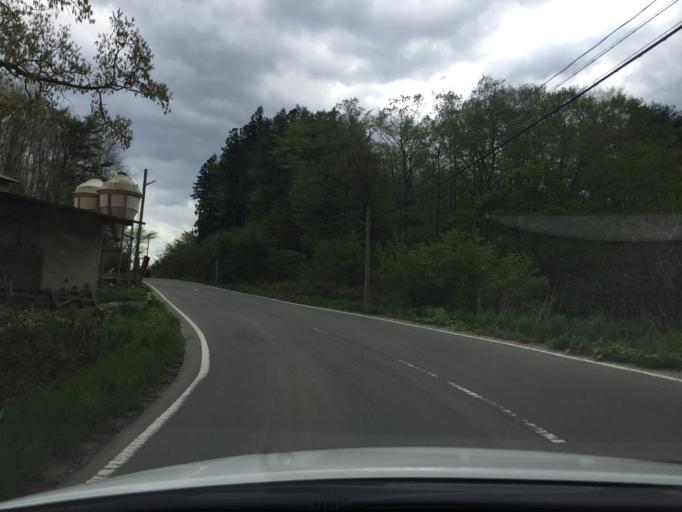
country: JP
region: Fukushima
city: Yanagawamachi-saiwaicho
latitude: 37.7053
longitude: 140.7475
